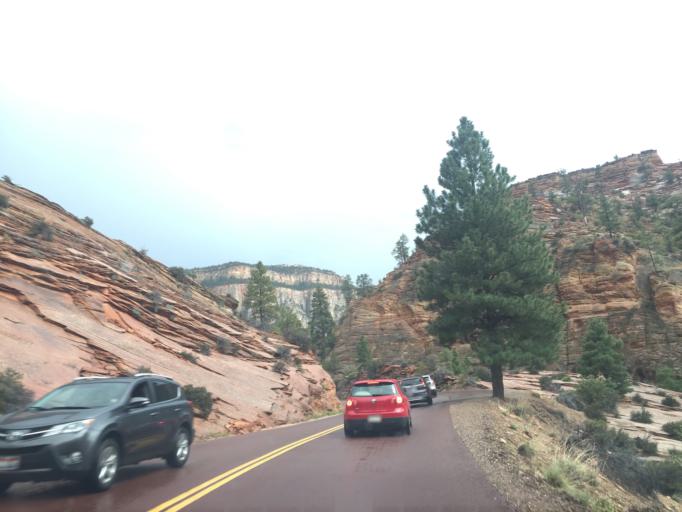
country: US
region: Utah
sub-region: Washington County
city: Hildale
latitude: 37.2246
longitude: -112.9015
